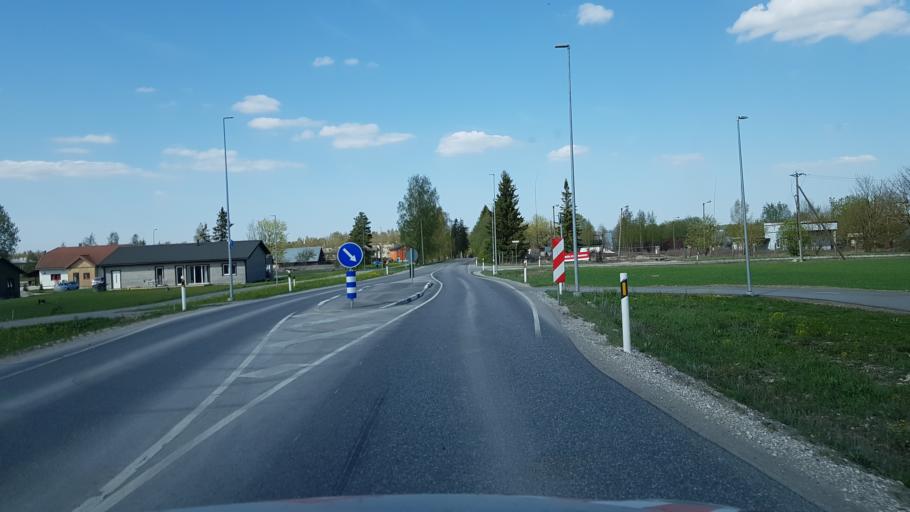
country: EE
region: Harju
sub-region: Rae vald
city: Vaida
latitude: 59.1986
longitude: 25.1048
